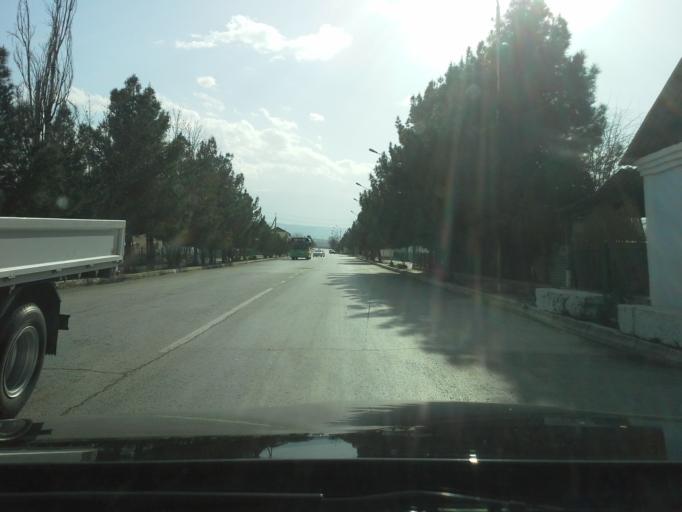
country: TM
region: Ahal
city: Ashgabat
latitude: 37.9886
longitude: 58.2863
